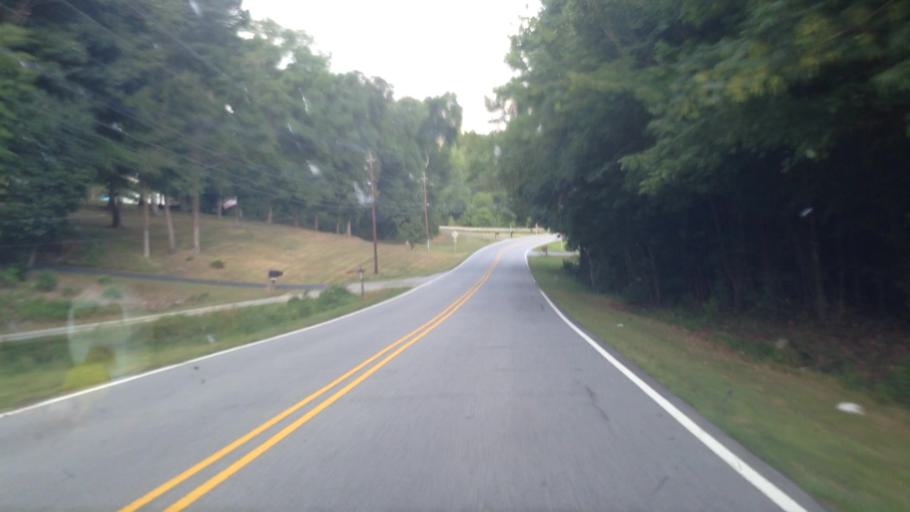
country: US
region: North Carolina
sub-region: Davidson County
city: Wallburg
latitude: 35.9661
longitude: -80.0813
